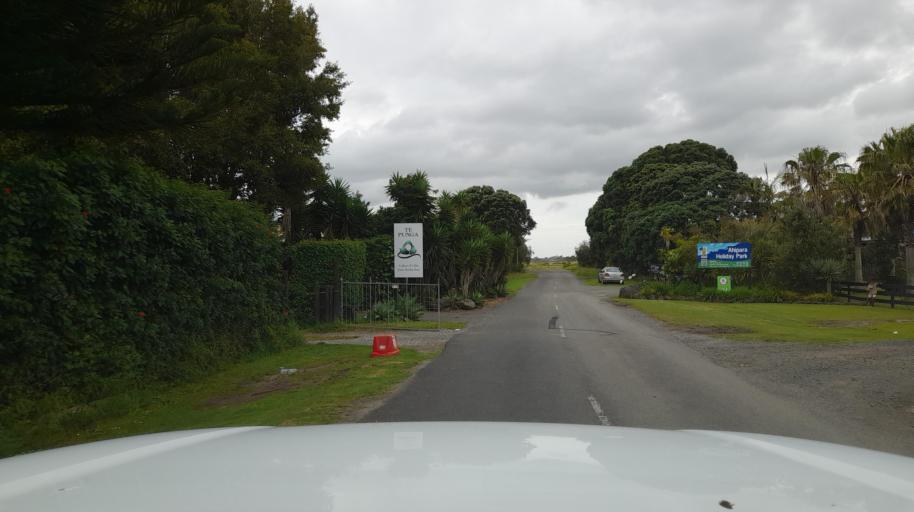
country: NZ
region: Northland
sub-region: Far North District
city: Ahipara
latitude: -35.1604
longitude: 173.1596
